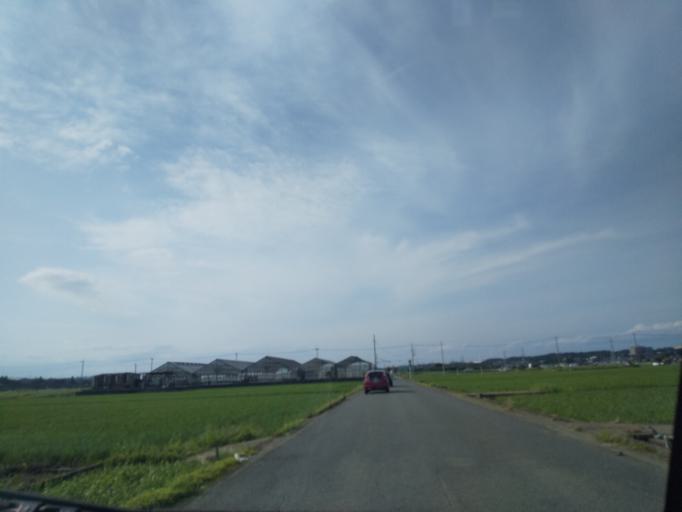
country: JP
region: Kanagawa
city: Zama
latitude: 35.4817
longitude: 139.3815
